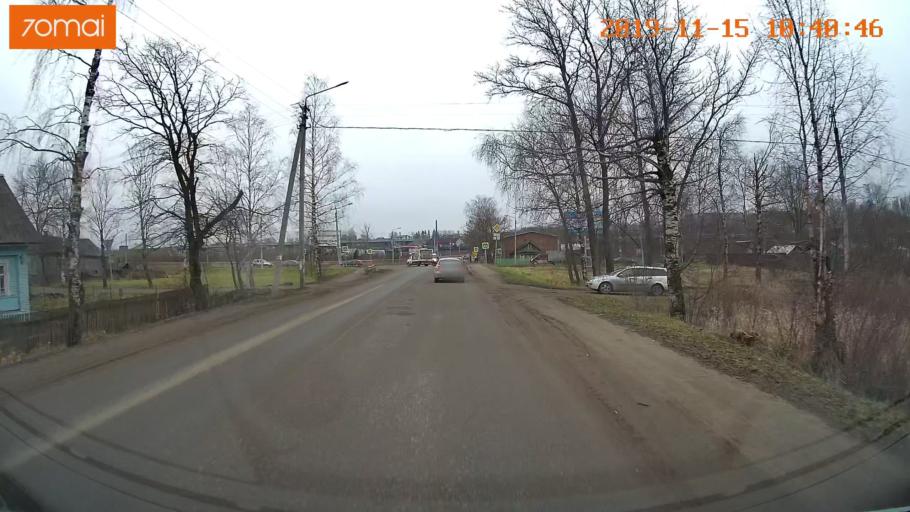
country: RU
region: Vologda
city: Sheksna
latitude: 59.2123
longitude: 38.5106
